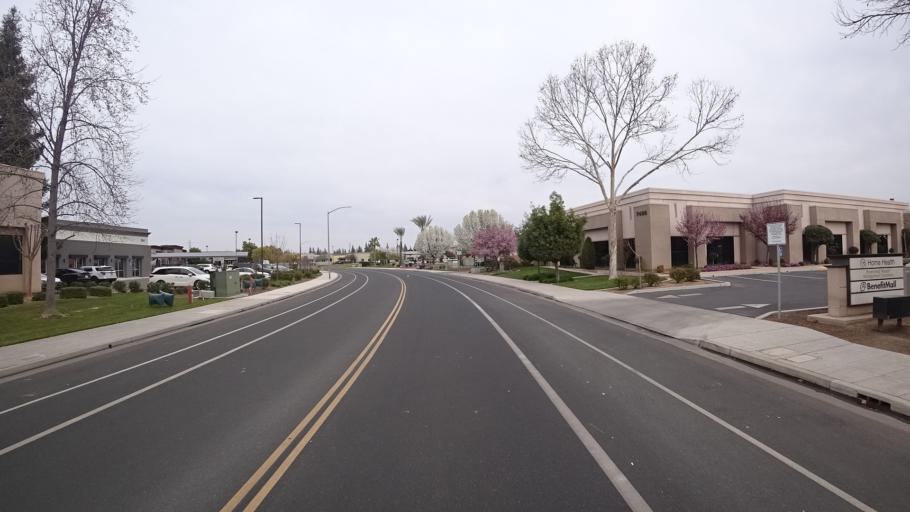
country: US
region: California
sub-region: Fresno County
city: Clovis
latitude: 36.8456
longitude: -119.8034
